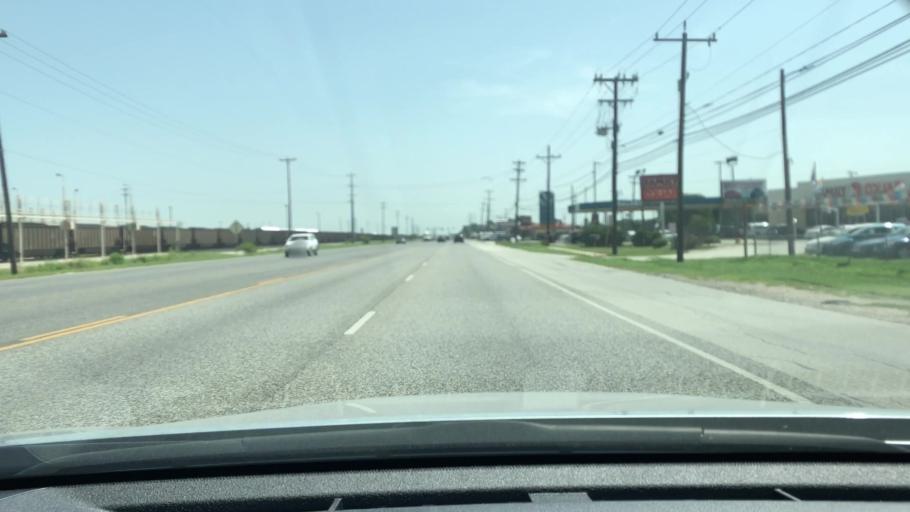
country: US
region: Texas
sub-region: Bexar County
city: Kirby
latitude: 29.4615
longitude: -98.4013
